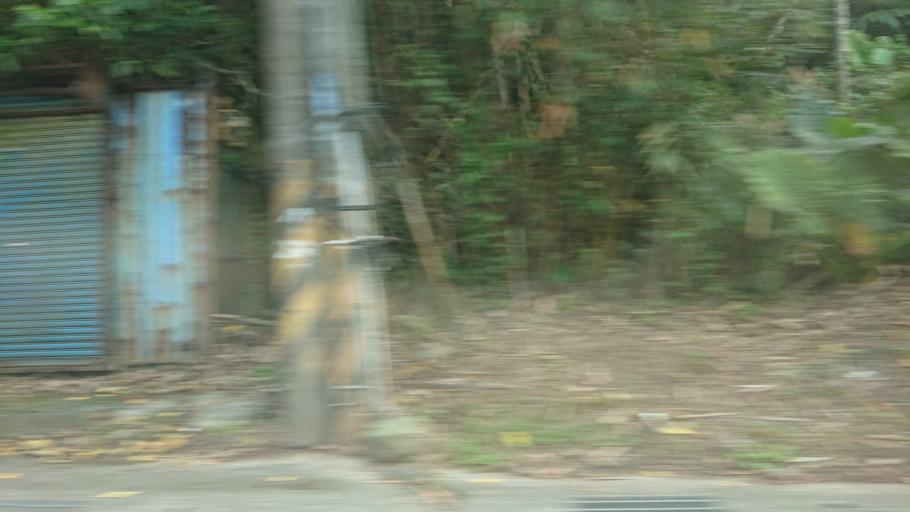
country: TW
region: Taiwan
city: Daxi
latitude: 24.8686
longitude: 121.4126
